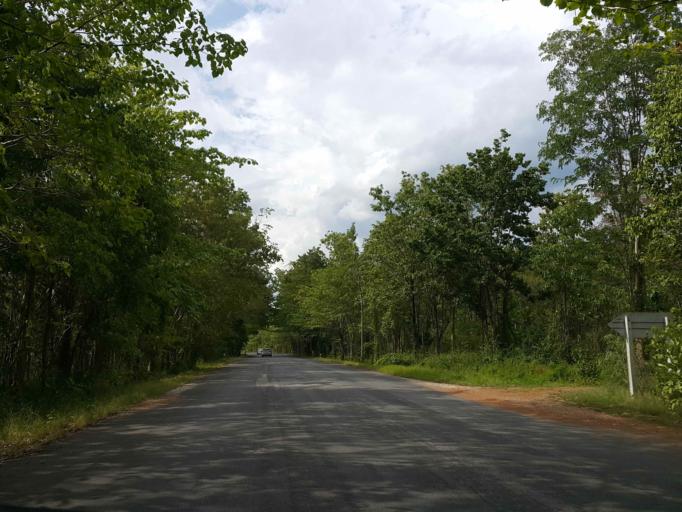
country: TH
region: Sukhothai
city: Thung Saliam
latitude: 17.4423
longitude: 99.3717
